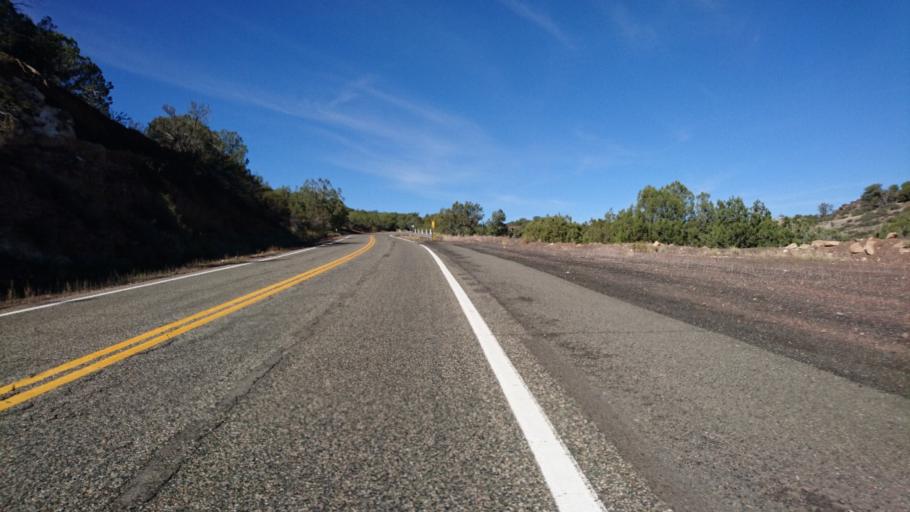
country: US
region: Arizona
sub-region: Yavapai County
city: Paulden
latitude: 35.2777
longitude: -112.6934
